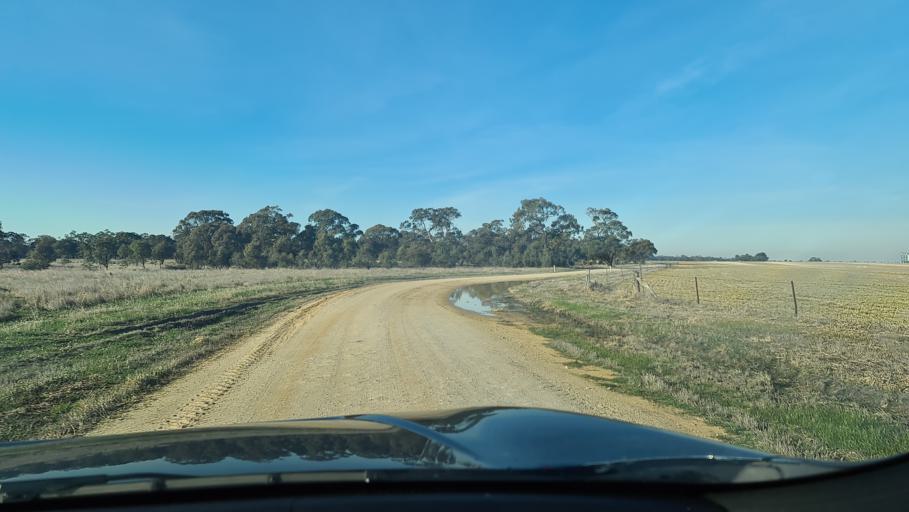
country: AU
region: Victoria
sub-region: Horsham
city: Horsham
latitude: -36.3566
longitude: 142.3962
